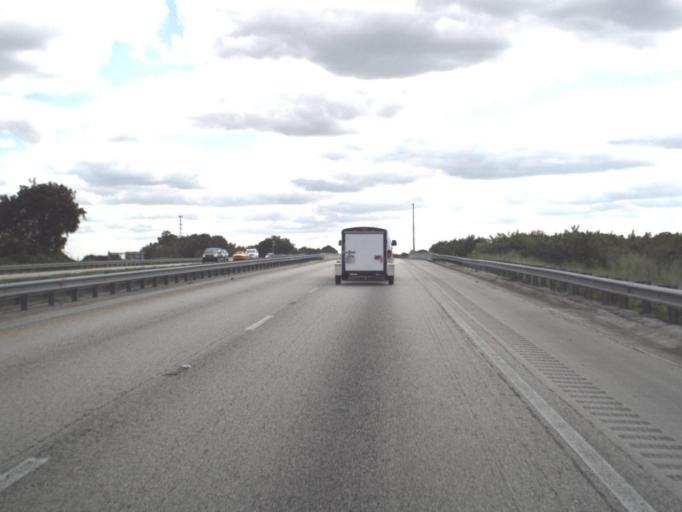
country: US
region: Florida
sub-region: Osceola County
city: Saint Cloud
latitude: 28.2669
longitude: -81.3338
